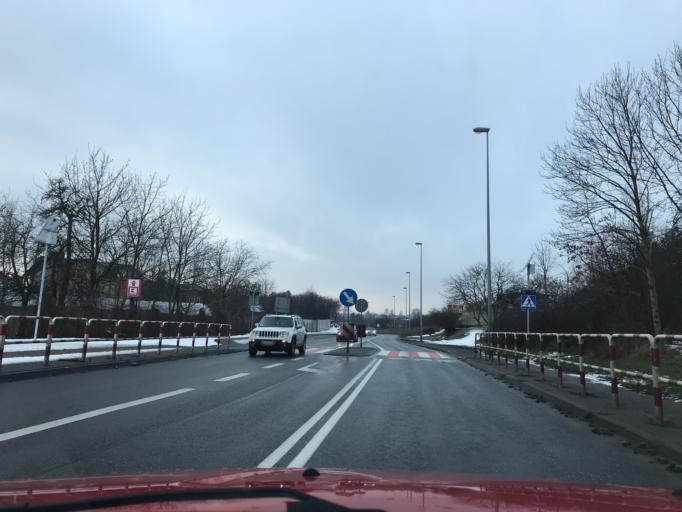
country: PL
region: Greater Poland Voivodeship
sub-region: Kalisz
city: Kalisz
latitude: 51.7722
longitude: 18.1006
